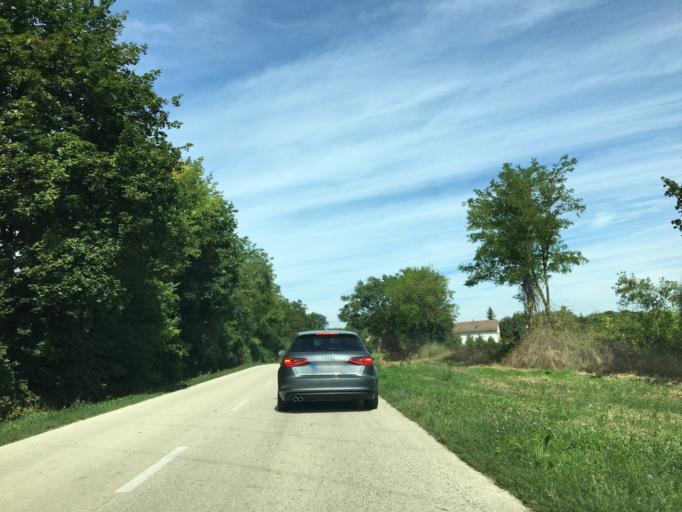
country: HU
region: Komarom-Esztergom
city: Bajna
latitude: 47.6425
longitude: 18.6060
